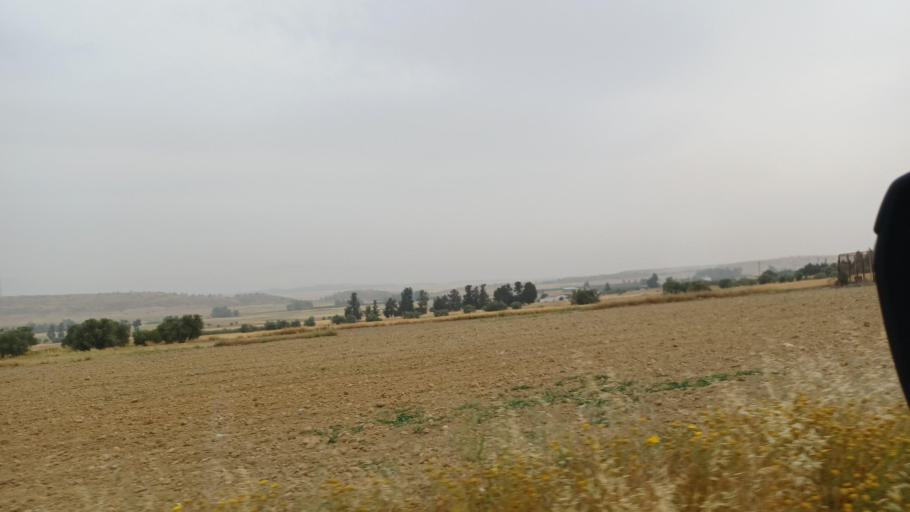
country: CY
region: Lefkosia
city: Mammari
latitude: 35.1774
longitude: 33.1978
